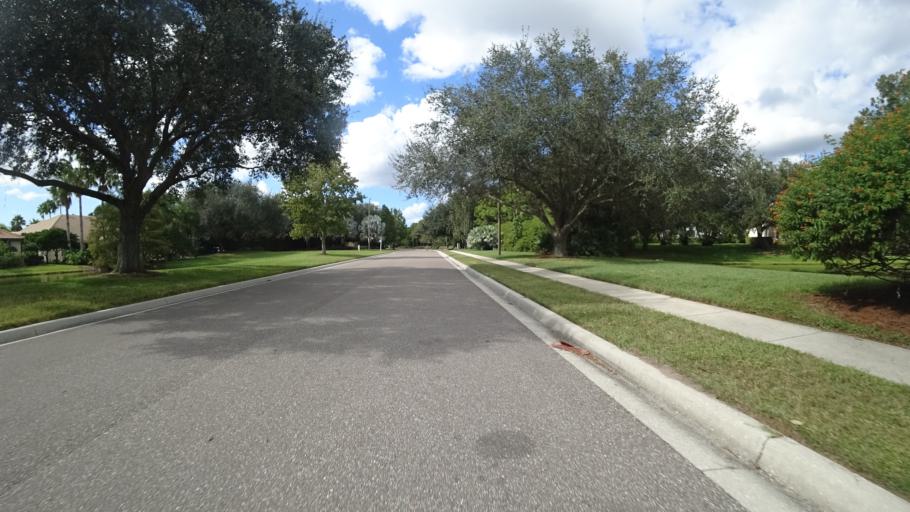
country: US
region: Florida
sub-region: Sarasota County
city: The Meadows
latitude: 27.3979
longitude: -82.4126
